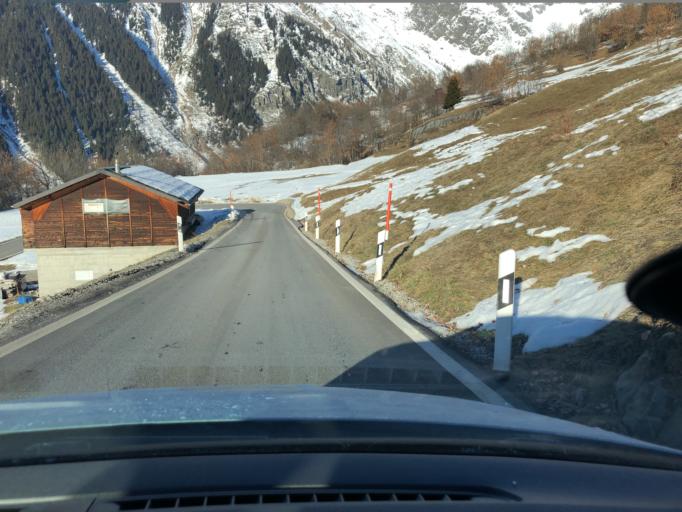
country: CH
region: Valais
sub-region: Goms District
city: Fiesch
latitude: 46.4283
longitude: 8.1511
